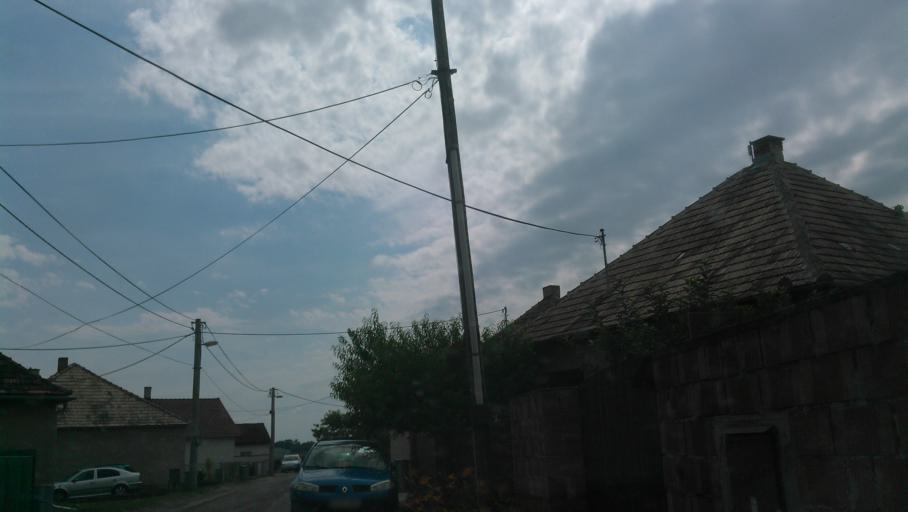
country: SK
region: Nitriansky
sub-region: Okres Nitra
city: Nitra
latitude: 48.5052
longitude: 18.0601
